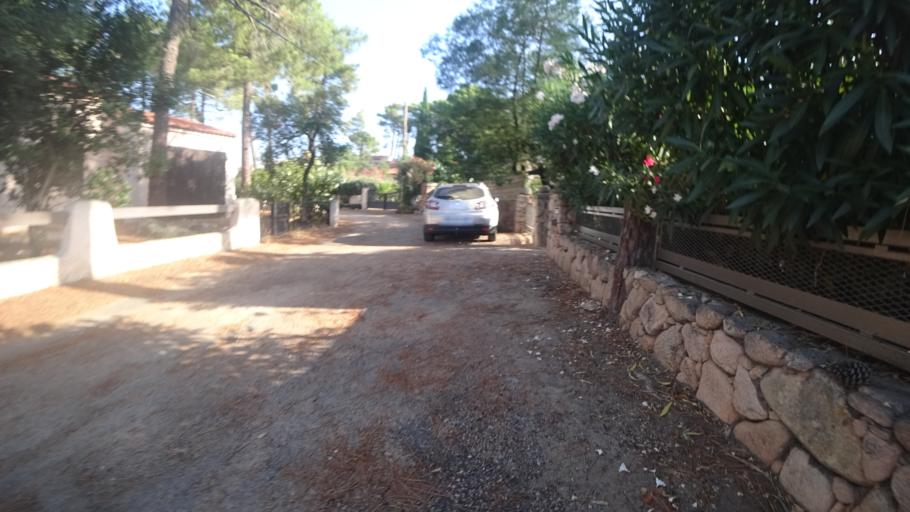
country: FR
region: Corsica
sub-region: Departement de la Corse-du-Sud
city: Porto-Vecchio
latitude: 41.6392
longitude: 9.3404
